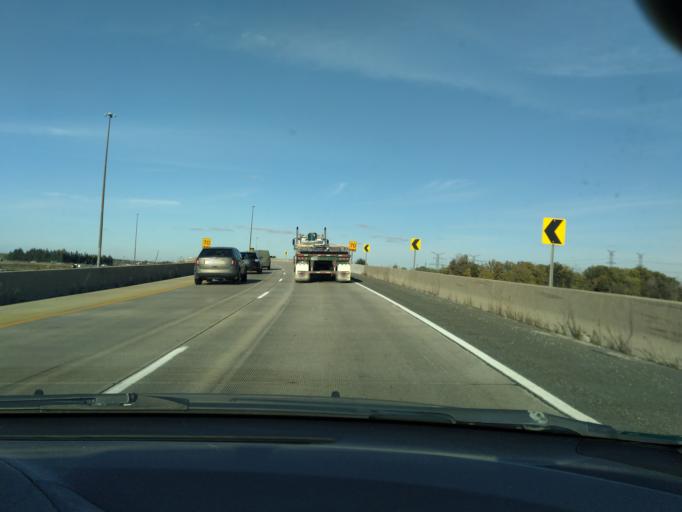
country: CA
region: Ontario
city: Brampton
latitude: 43.5951
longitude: -79.8002
